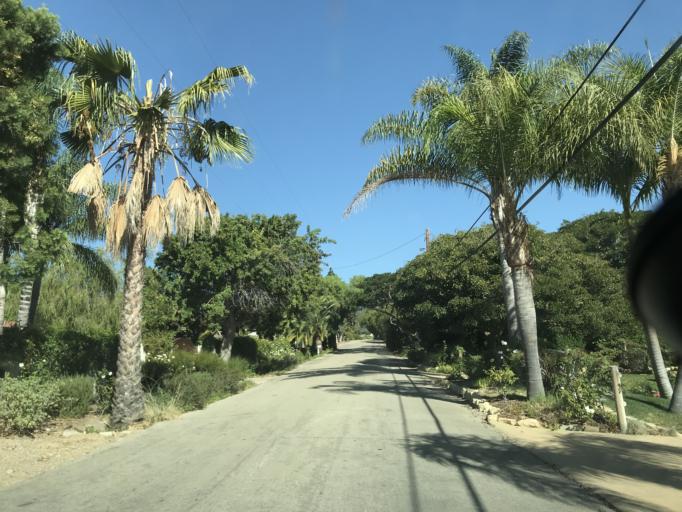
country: US
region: California
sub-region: Santa Barbara County
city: Goleta
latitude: 34.4541
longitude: -119.7861
